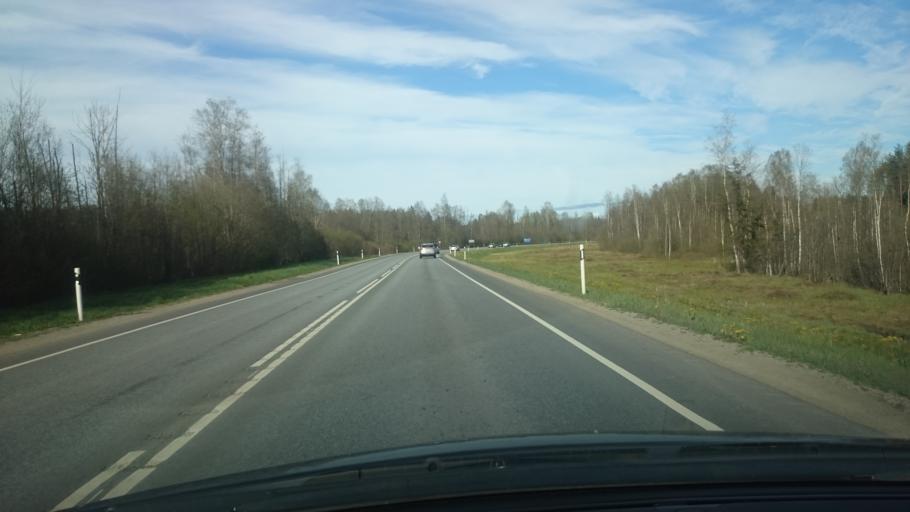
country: EE
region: Ida-Virumaa
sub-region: Toila vald
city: Toila
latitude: 59.3729
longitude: 27.4935
